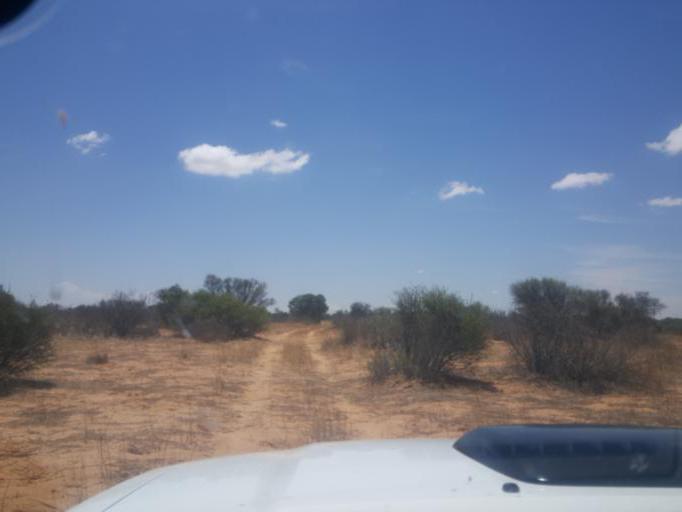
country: BW
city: Lokwabe
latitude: -24.9111
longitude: 21.4177
